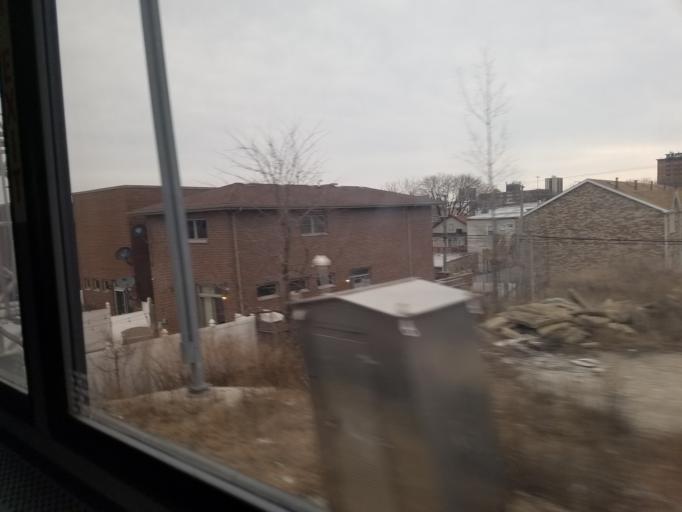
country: US
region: Illinois
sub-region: Cook County
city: Chicago
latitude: 41.8345
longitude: -87.6353
